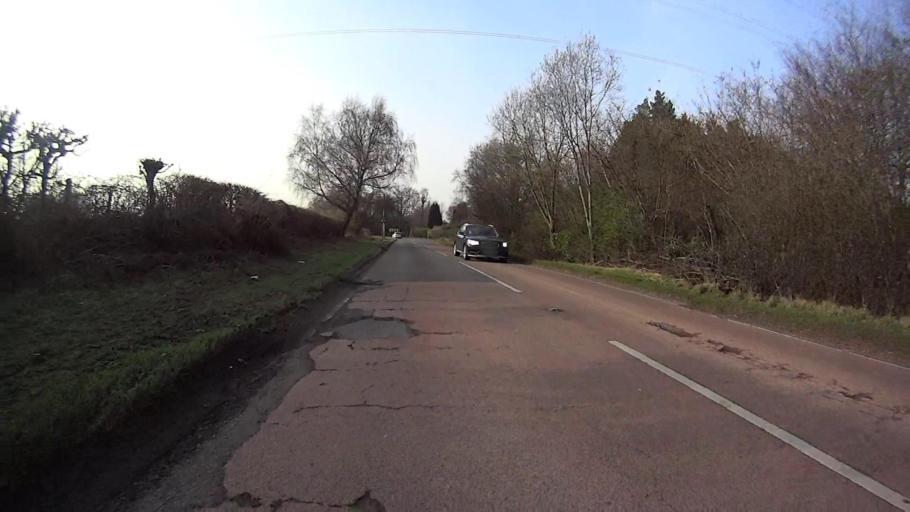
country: GB
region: England
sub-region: West Sussex
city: Copthorne
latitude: 51.1143
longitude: -0.1238
